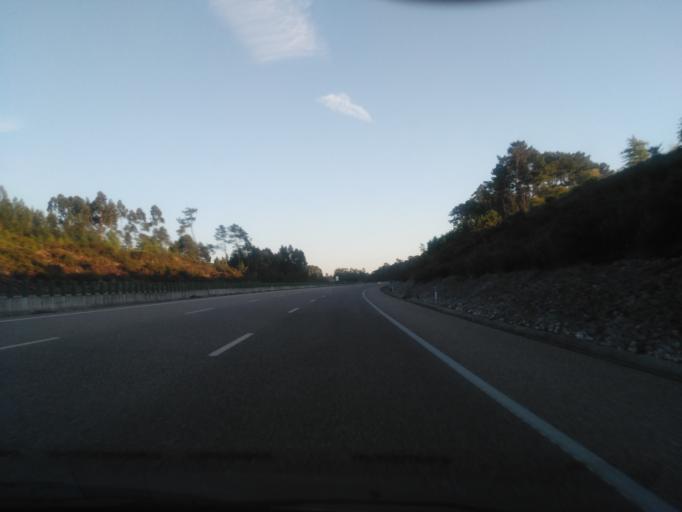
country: PT
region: Leiria
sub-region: Pombal
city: Lourical
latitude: 39.9772
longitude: -8.7831
